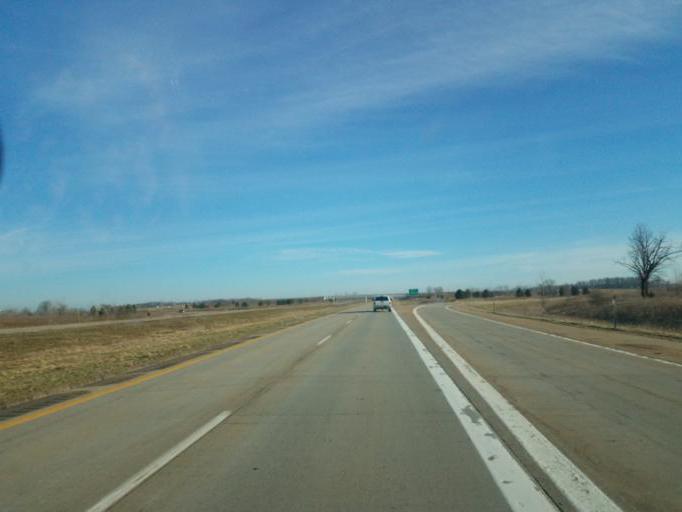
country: US
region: Michigan
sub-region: Gratiot County
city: Ithaca
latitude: 43.1705
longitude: -84.5636
